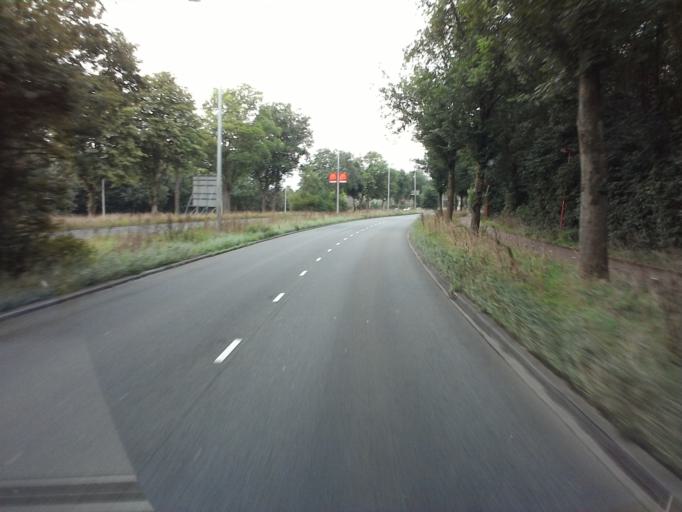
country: NL
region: Utrecht
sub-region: Gemeente Utrecht
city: Utrecht
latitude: 52.1280
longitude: 5.1046
